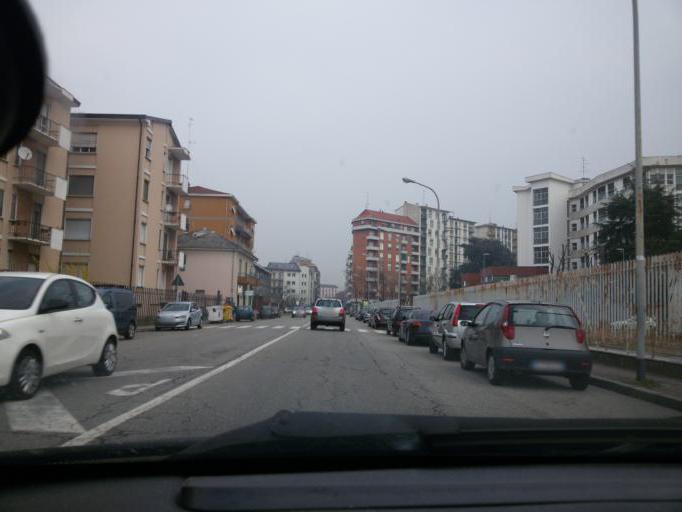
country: IT
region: Piedmont
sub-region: Provincia di Vercelli
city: Vercelli
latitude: 45.3174
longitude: 8.4113
